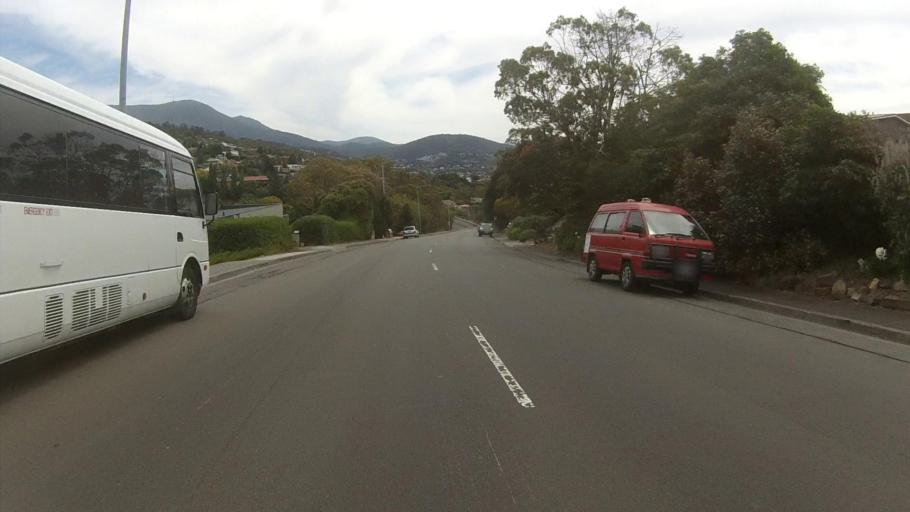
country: AU
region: Tasmania
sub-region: Hobart
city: Sandy Bay
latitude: -42.9142
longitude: 147.3418
